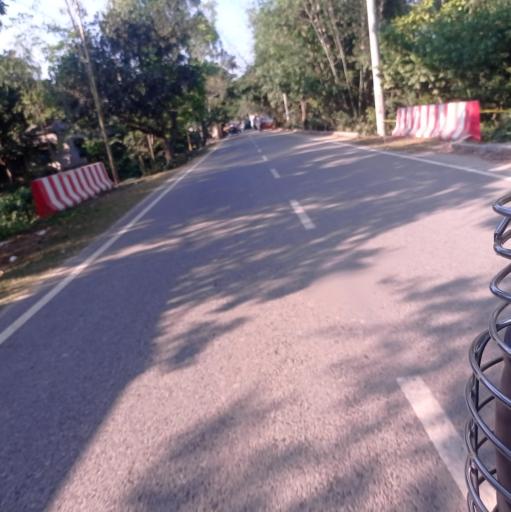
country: BD
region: Dhaka
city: Bajitpur
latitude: 24.1554
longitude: 90.8110
